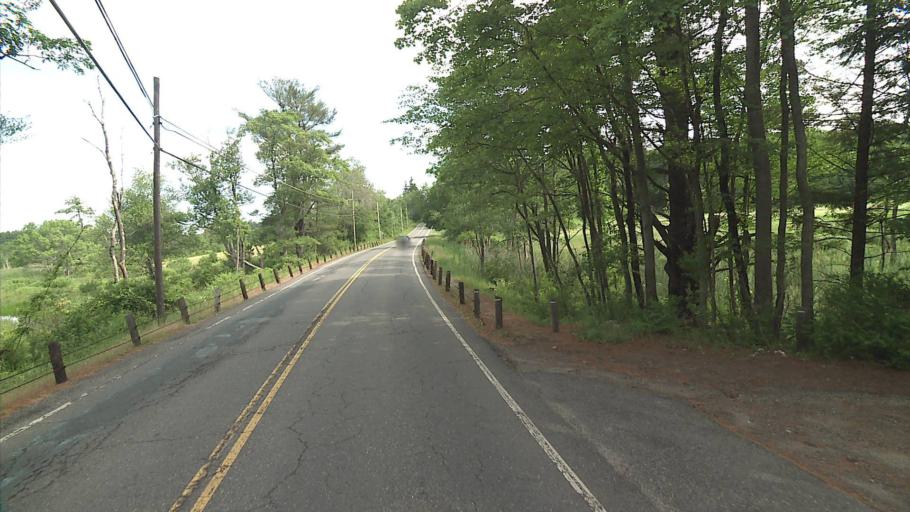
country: US
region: Connecticut
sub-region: Litchfield County
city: Litchfield
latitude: 41.7150
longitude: -73.1865
